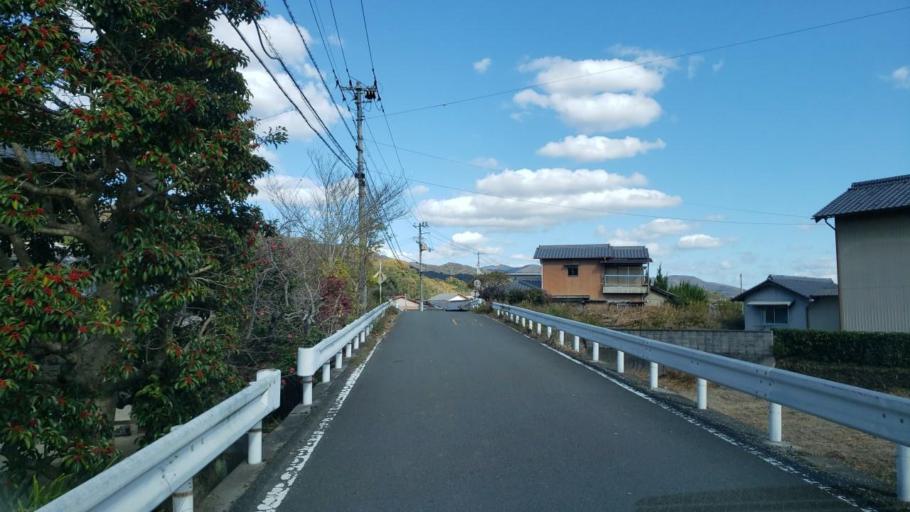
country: JP
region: Tokushima
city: Wakimachi
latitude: 34.0773
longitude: 134.1948
